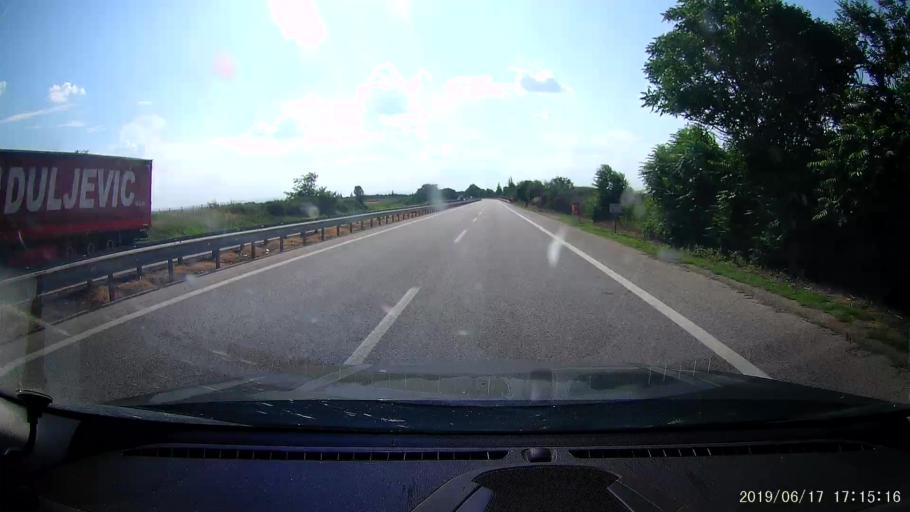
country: GR
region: East Macedonia and Thrace
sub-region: Nomos Evrou
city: Kastanies
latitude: 41.7014
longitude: 26.5002
